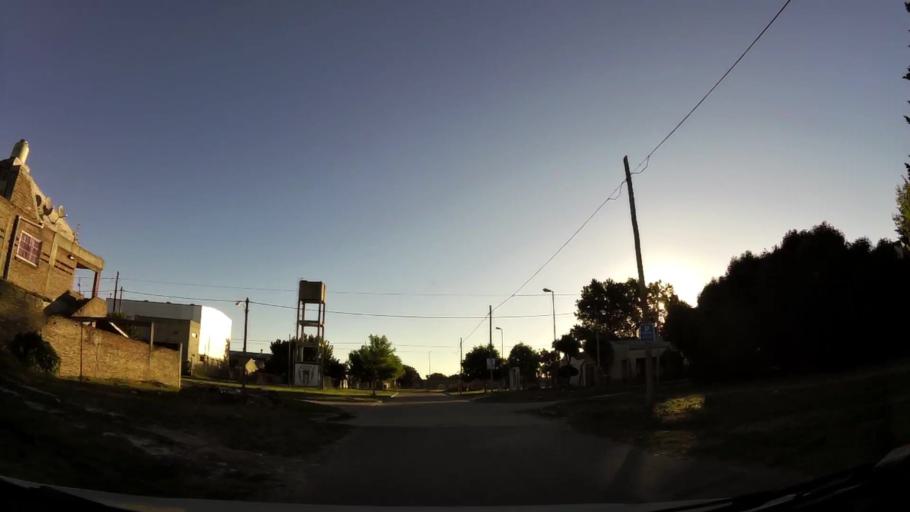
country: AR
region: Buenos Aires
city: San Justo
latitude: -34.7215
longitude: -58.6098
